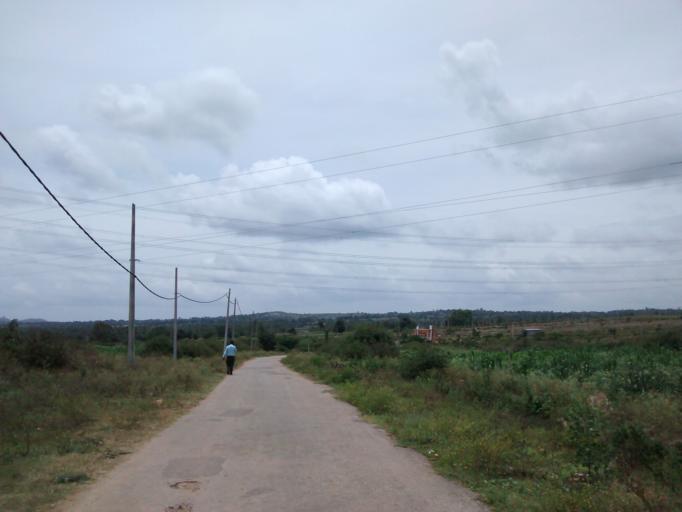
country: IN
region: Karnataka
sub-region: Hassan
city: Hassan
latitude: 12.9228
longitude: 76.1320
